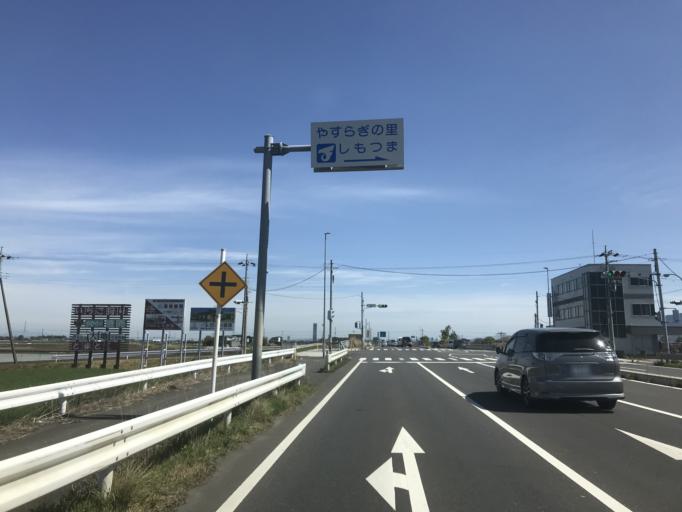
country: JP
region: Ibaraki
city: Ishige
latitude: 36.1474
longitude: 139.9906
